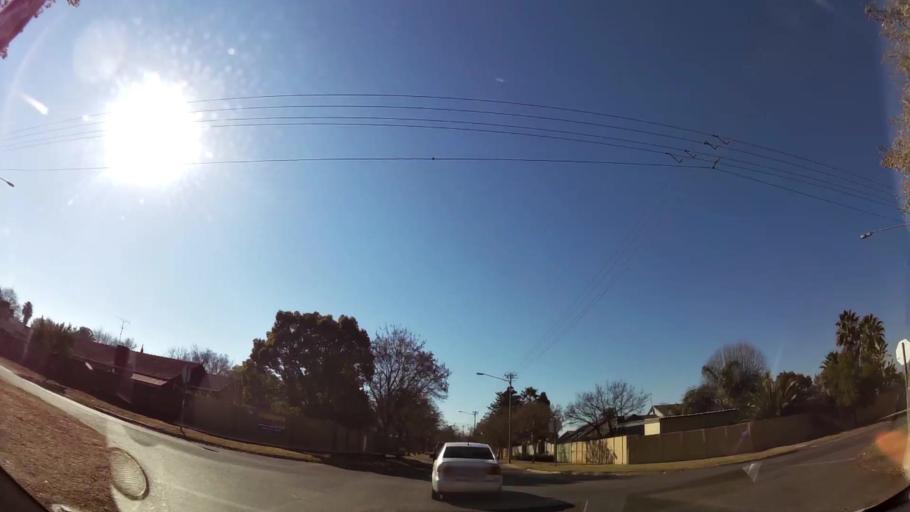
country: ZA
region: Gauteng
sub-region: City of Tshwane Metropolitan Municipality
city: Centurion
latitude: -25.8545
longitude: 28.2095
